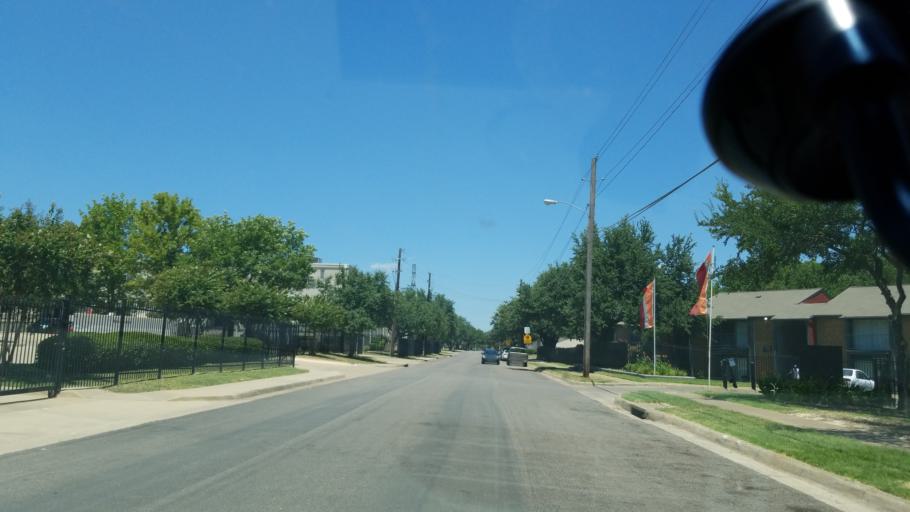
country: US
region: Texas
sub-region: Dallas County
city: Cockrell Hill
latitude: 32.6995
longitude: -96.8300
